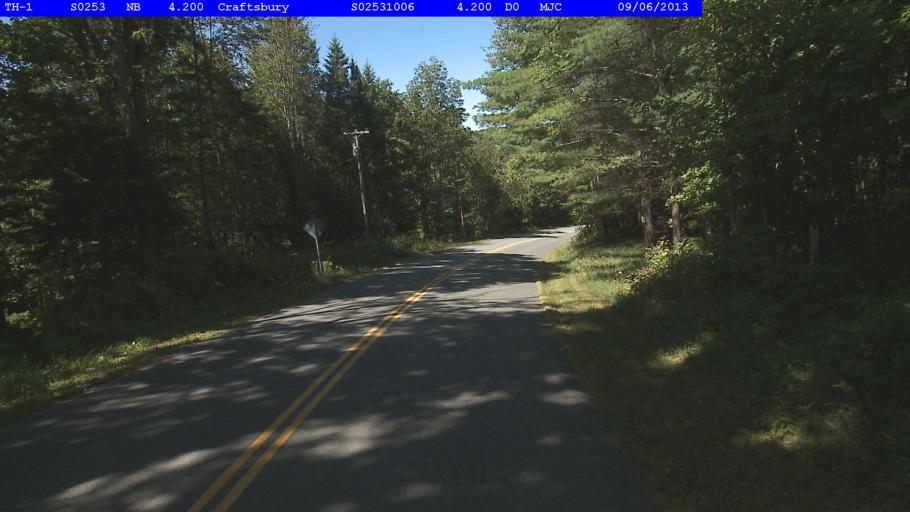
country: US
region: Vermont
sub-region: Caledonia County
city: Hardwick
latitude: 44.6668
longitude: -72.3877
